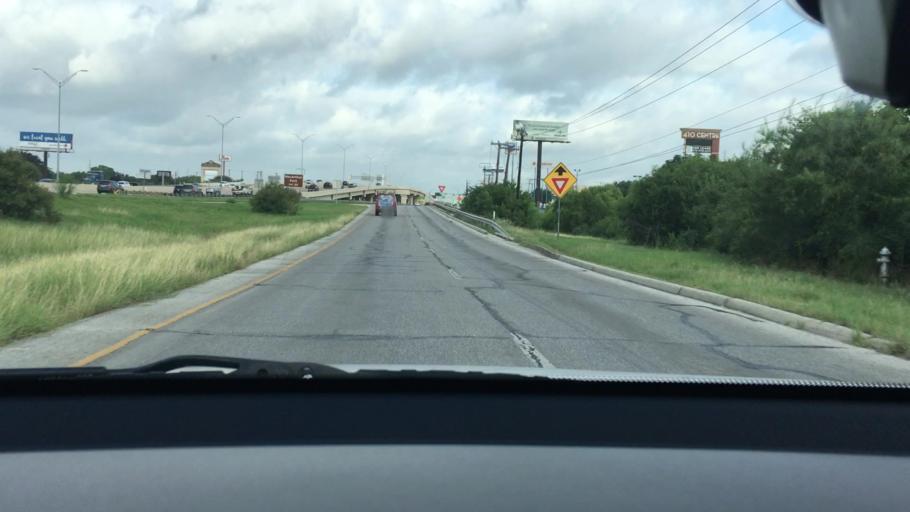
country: US
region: Texas
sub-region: Bexar County
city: Windcrest
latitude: 29.5165
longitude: -98.4066
